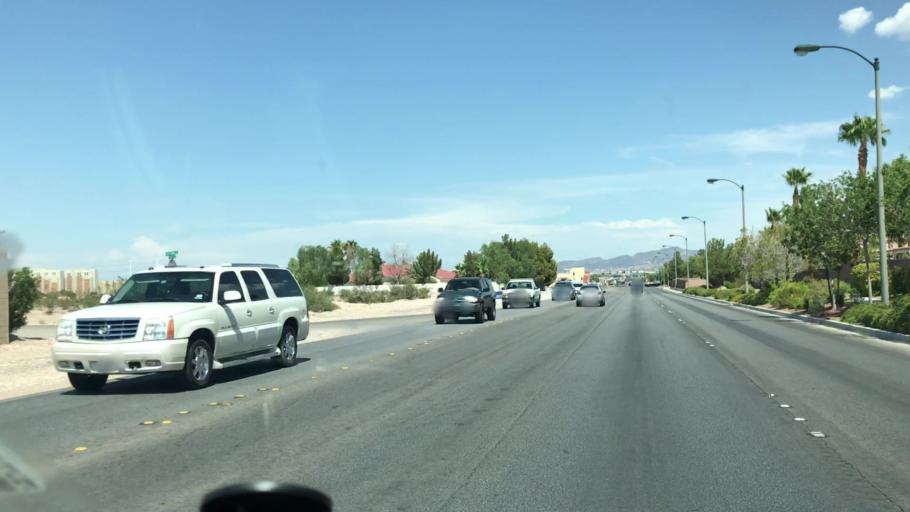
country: US
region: Nevada
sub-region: Clark County
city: Enterprise
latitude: 35.9988
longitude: -115.1945
